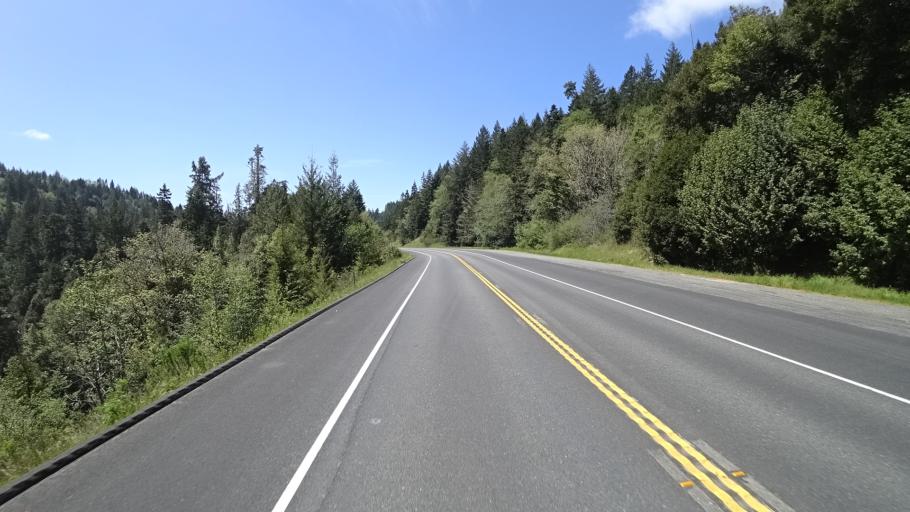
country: US
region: California
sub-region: Humboldt County
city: Blue Lake
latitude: 40.8989
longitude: -123.9243
